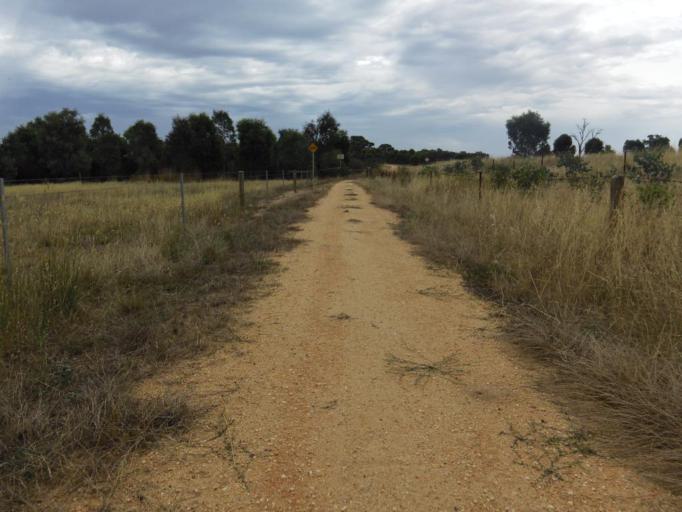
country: AU
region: Victoria
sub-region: Greater Bendigo
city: Kennington
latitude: -36.8245
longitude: 144.5824
